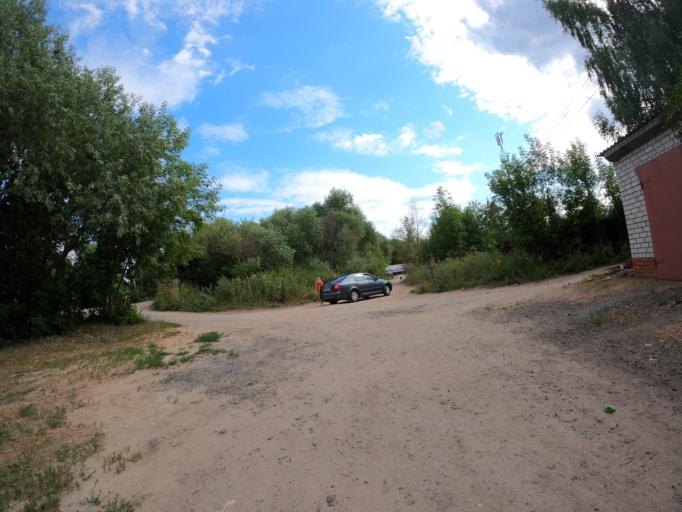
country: RU
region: Moskovskaya
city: Bronnitsy
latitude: 55.4823
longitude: 38.2350
